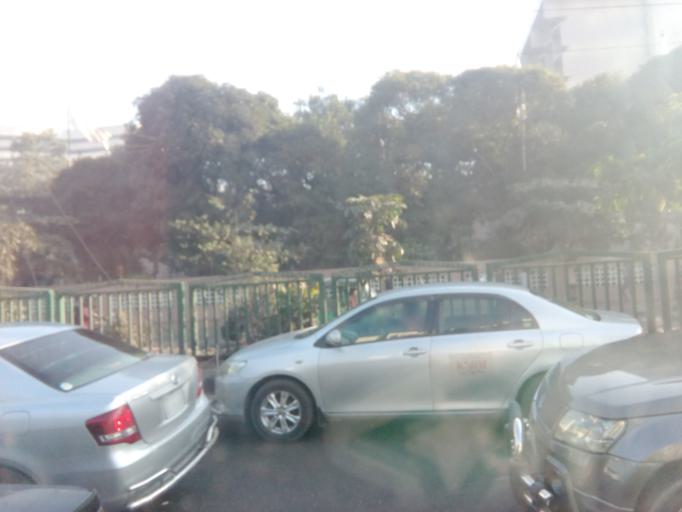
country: BD
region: Dhaka
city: Azimpur
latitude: 23.7492
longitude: 90.3937
